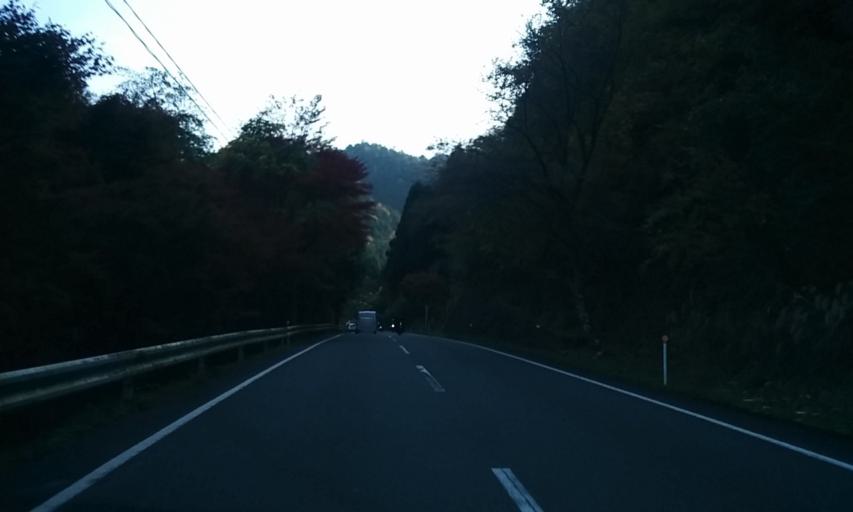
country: JP
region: Kyoto
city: Kameoka
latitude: 35.2432
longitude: 135.5588
